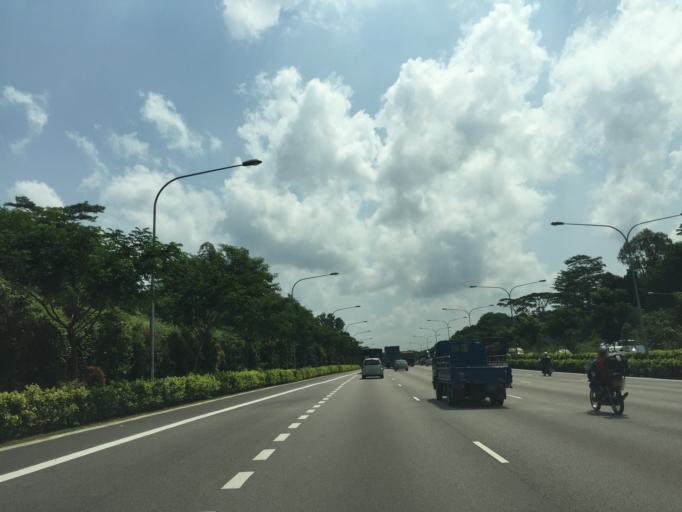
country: SG
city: Singapore
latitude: 1.3410
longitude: 103.8043
